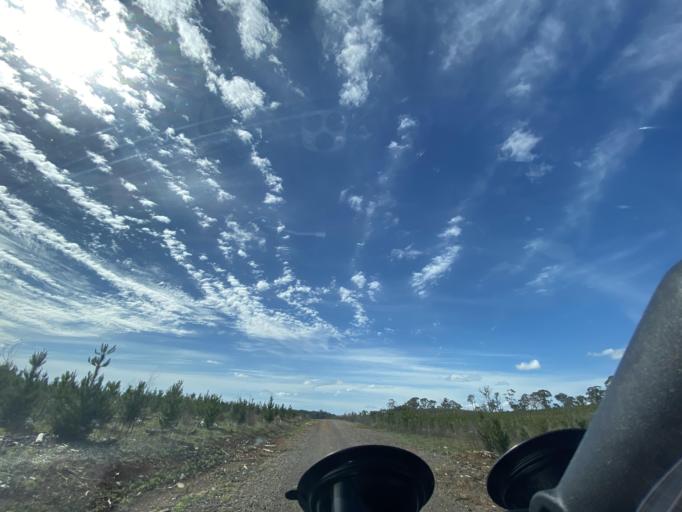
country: AU
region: Victoria
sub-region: Mansfield
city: Mansfield
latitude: -36.8267
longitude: 146.1032
